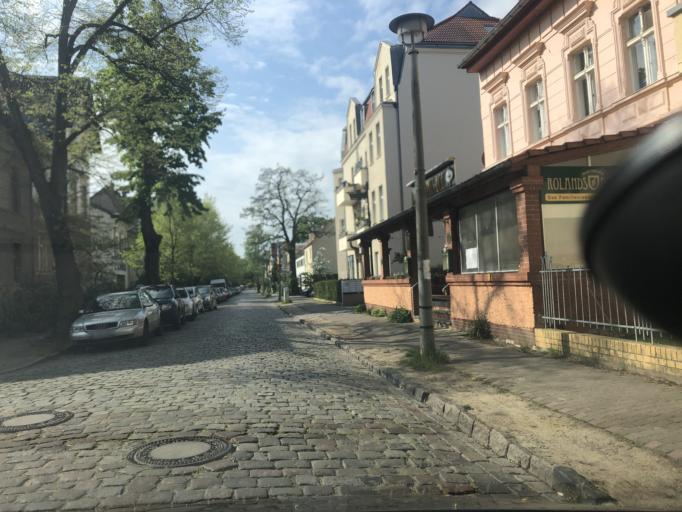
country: DE
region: Berlin
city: Friedrichshagen
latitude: 52.4532
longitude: 13.6279
